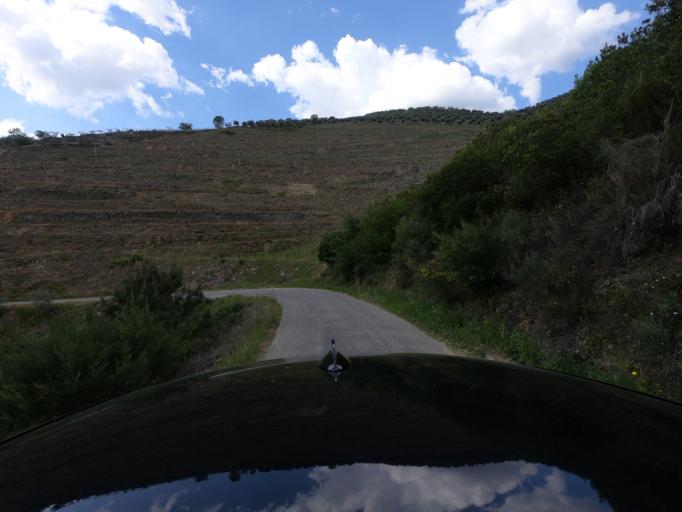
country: PT
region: Vila Real
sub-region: Sabrosa
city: Vilela
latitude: 41.2000
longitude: -7.6577
